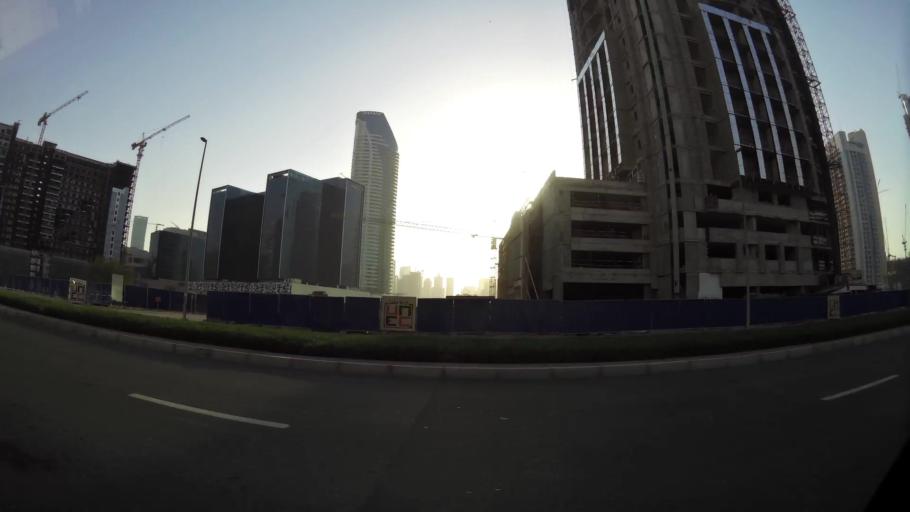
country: AE
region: Dubai
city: Dubai
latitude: 25.1883
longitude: 55.2838
